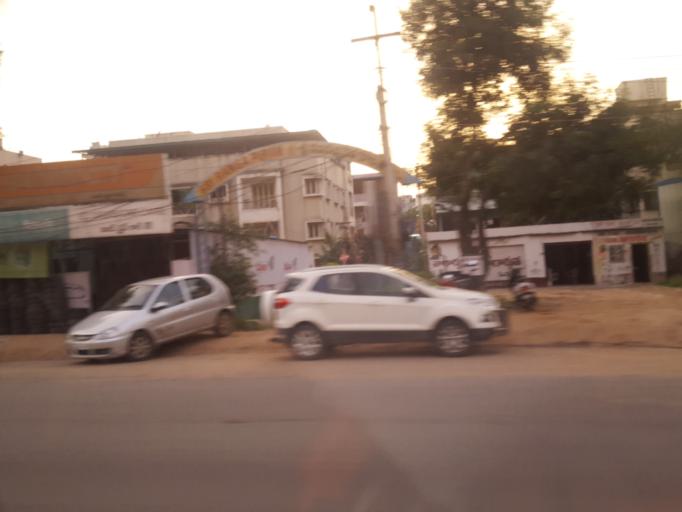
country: IN
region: Telangana
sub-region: Rangareddi
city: Kukatpalli
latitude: 17.5046
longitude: 78.3621
